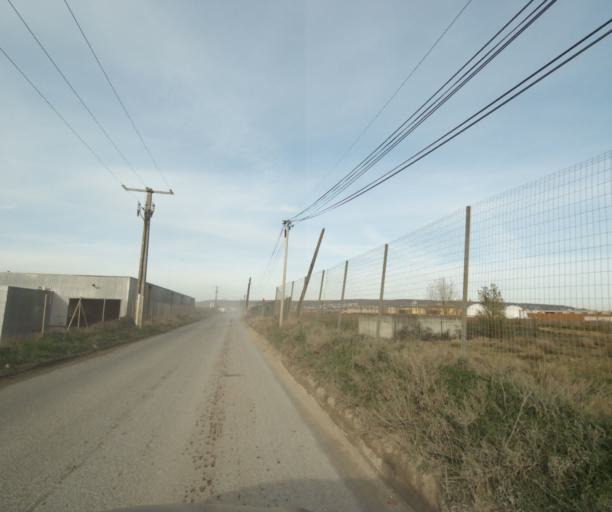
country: FR
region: Ile-de-France
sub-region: Departement des Yvelines
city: Medan
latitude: 48.9494
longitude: 2.0119
